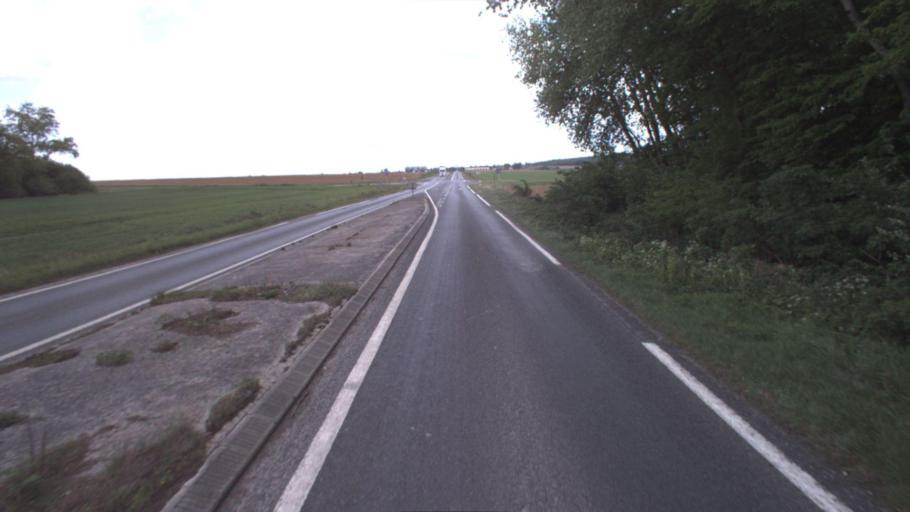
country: FR
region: Ile-de-France
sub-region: Departement de Seine-et-Marne
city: Saint-Pathus
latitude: 49.0540
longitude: 2.7851
